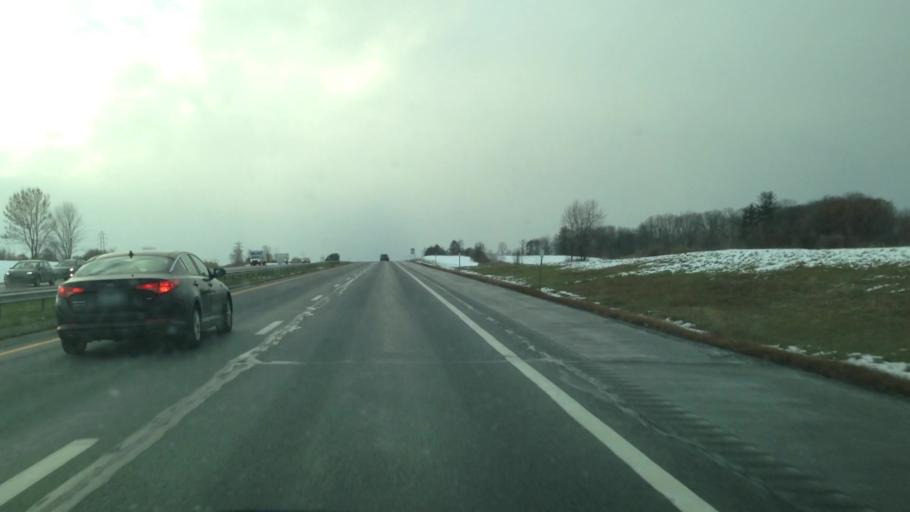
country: US
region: New York
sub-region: Montgomery County
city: Amsterdam
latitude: 42.9298
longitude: -74.2277
